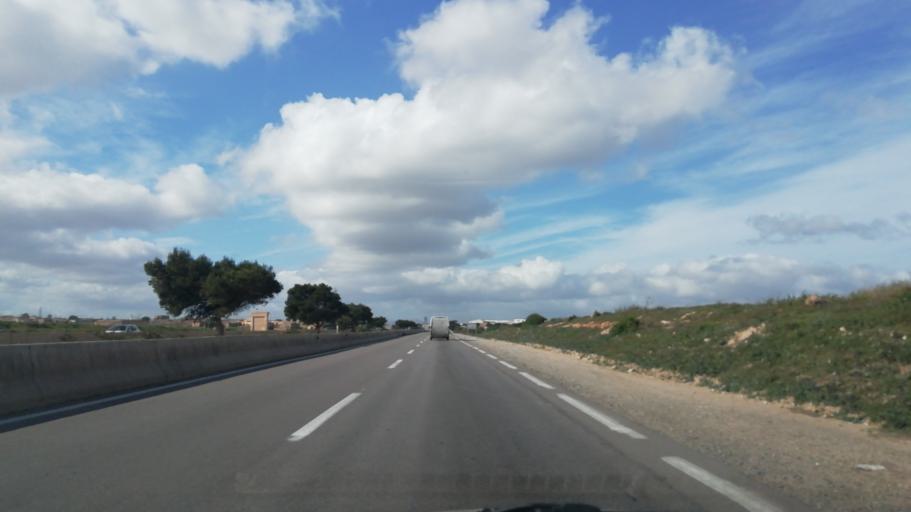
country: DZ
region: Oran
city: Ain el Bya
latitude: 35.7670
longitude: -0.2147
